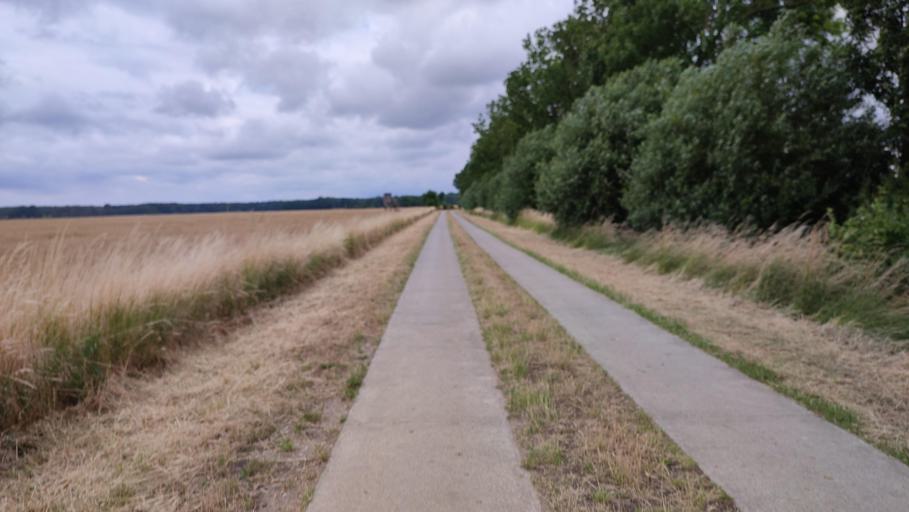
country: DE
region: Lower Saxony
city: Hitzacker
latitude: 53.1724
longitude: 11.1019
